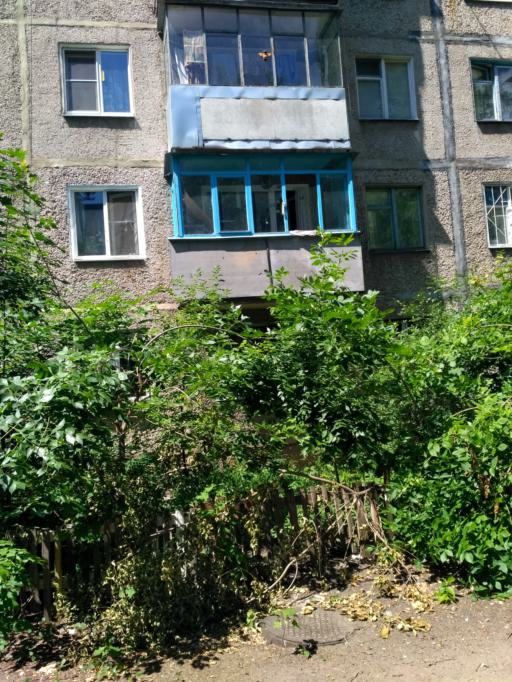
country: RU
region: Voronezj
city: Voronezh
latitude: 51.6456
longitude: 39.1461
